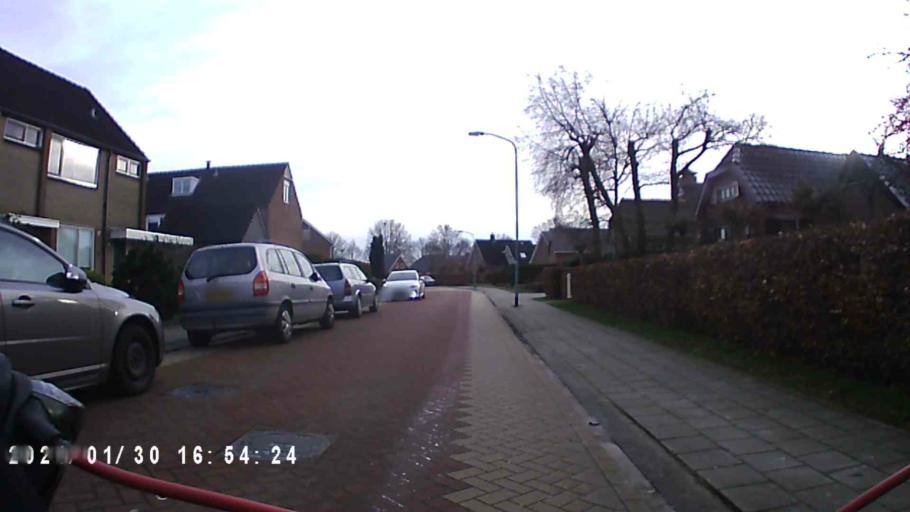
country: NL
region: Groningen
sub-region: Gemeente Leek
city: Leek
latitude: 53.1565
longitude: 6.3817
